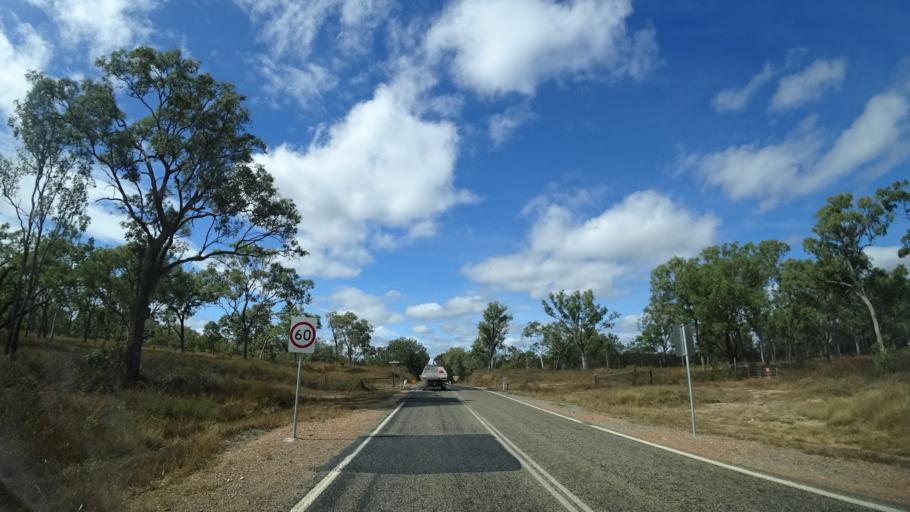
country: AU
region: Queensland
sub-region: Cairns
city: Port Douglas
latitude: -16.4979
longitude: 145.0004
